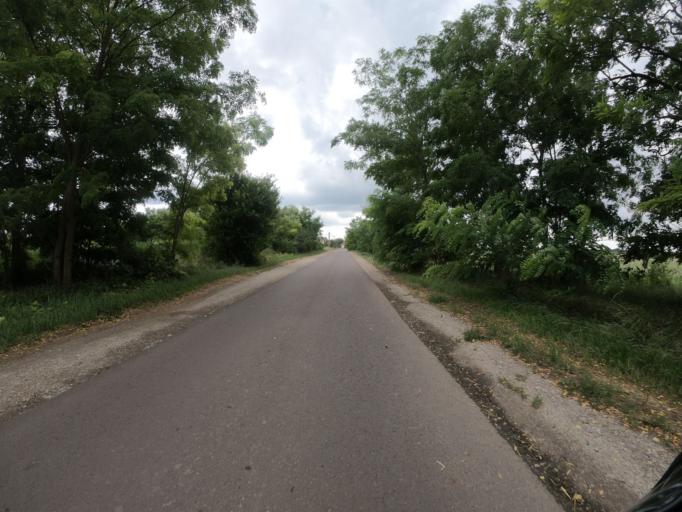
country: HU
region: Heves
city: Poroszlo
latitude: 47.7054
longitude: 20.7008
